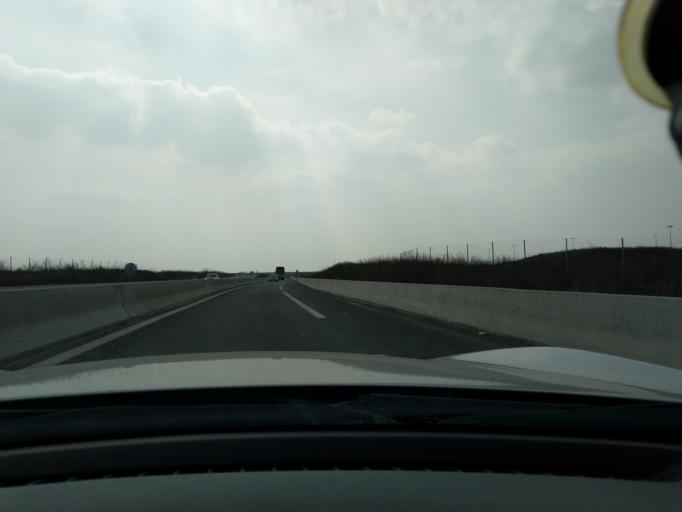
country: FR
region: Ile-de-France
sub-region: Departement du Val-d'Oise
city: Roissy-en-France
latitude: 49.0320
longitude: 2.5419
